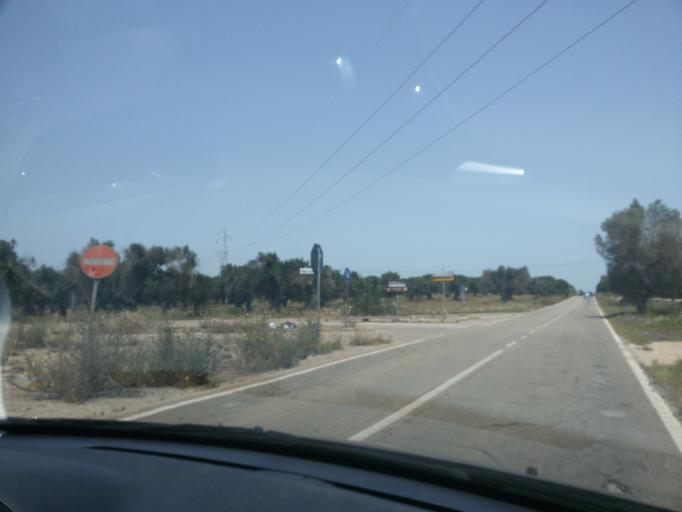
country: IT
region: Apulia
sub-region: Provincia di Lecce
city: Porto Cesareo
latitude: 40.2894
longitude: 17.9125
